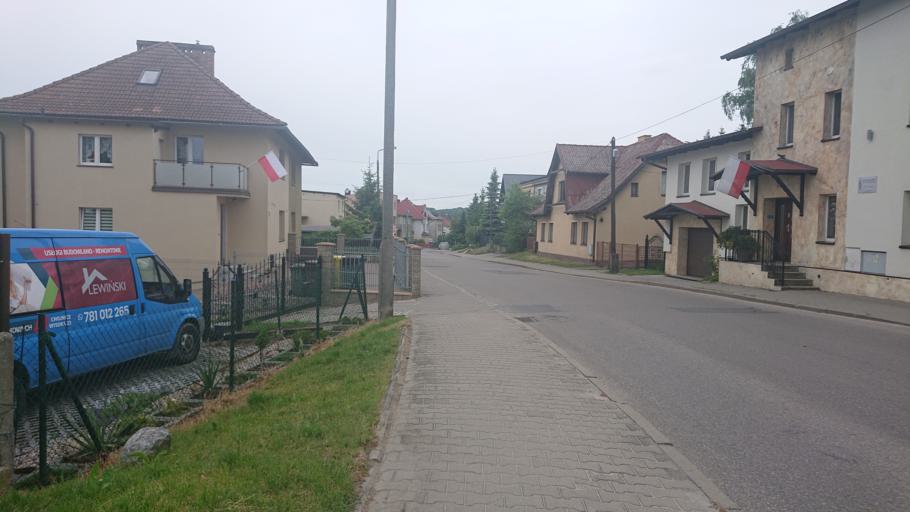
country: PL
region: Pomeranian Voivodeship
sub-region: Powiat chojnicki
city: Chojnice
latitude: 53.6969
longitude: 17.5666
